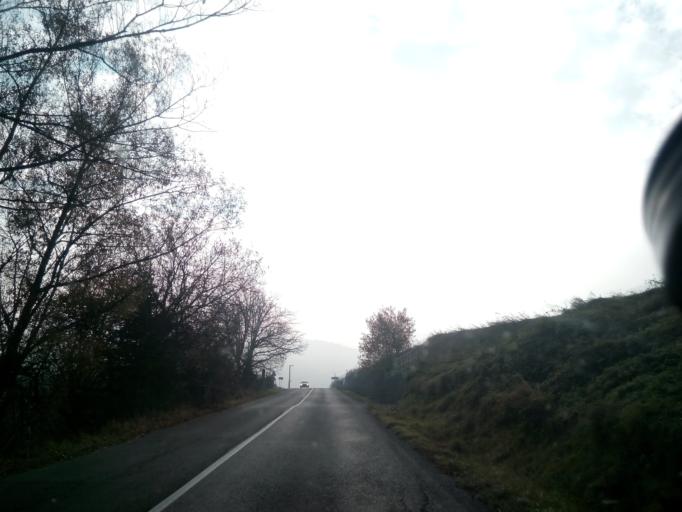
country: SK
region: Kosicky
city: Gelnica
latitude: 48.8608
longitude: 21.0108
